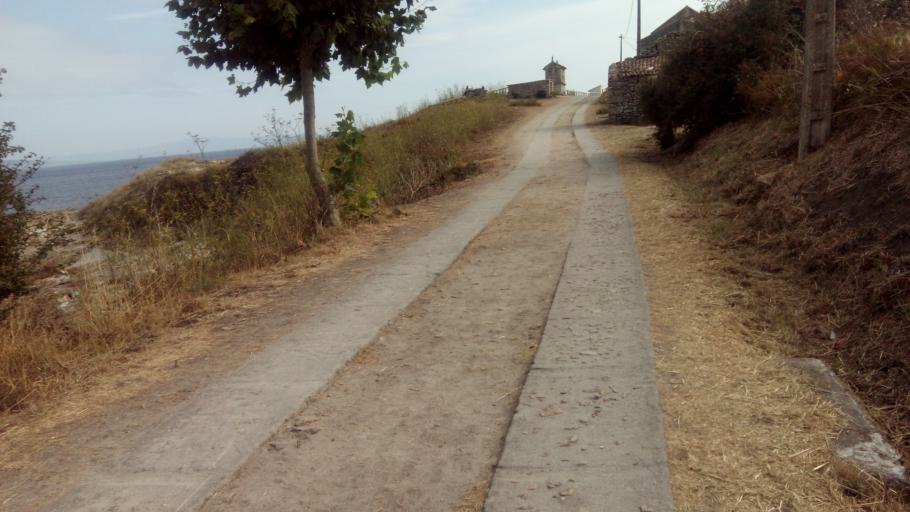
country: ES
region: Galicia
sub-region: Provincia de Pontevedra
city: Sanxenxo
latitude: 42.3717
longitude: -8.9334
